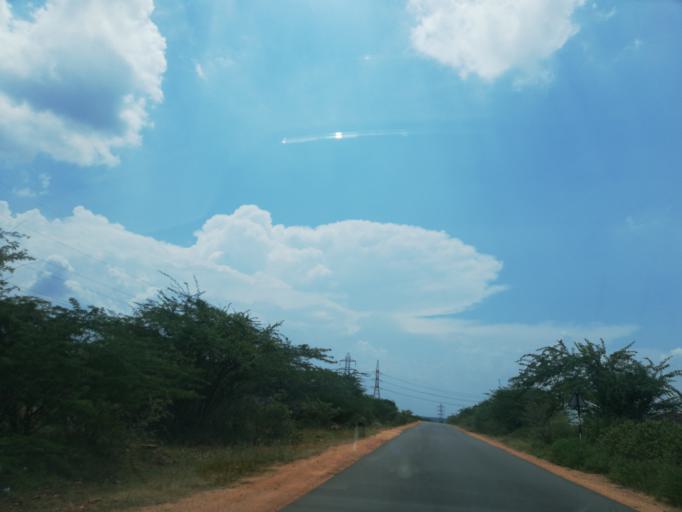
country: IN
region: Andhra Pradesh
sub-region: Guntur
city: Macherla
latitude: 16.5683
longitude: 79.3432
